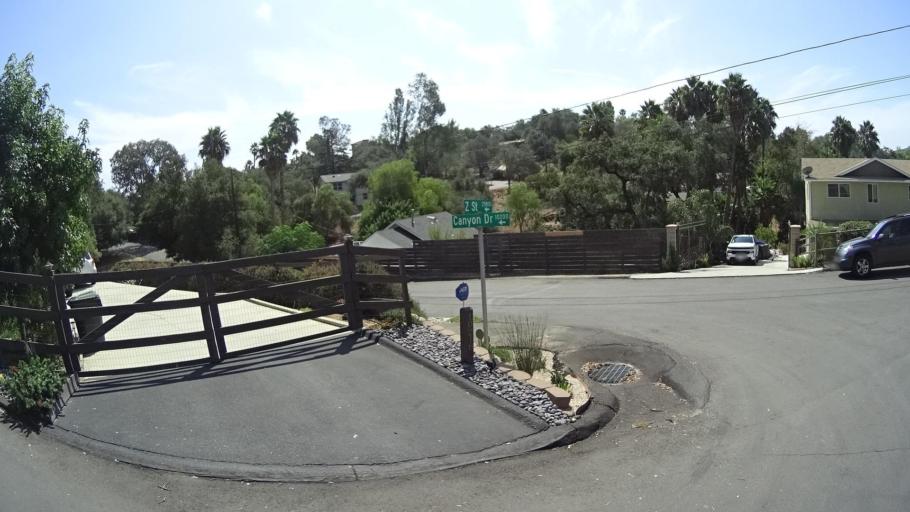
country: US
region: California
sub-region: San Diego County
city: Hidden Meadows
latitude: 33.1811
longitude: -117.1088
